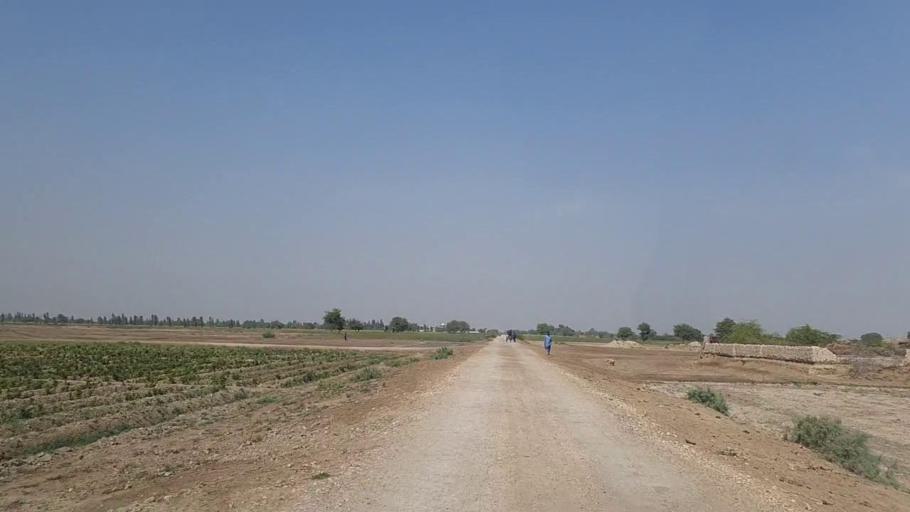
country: PK
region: Sindh
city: Samaro
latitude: 25.2592
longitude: 69.3947
